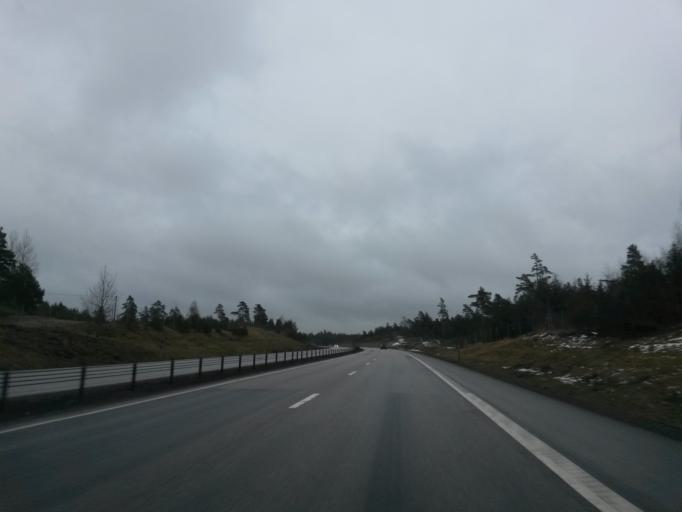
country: SE
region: Vaestra Goetaland
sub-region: Uddevalla Kommun
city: Uddevalla
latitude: 58.3300
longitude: 12.0250
